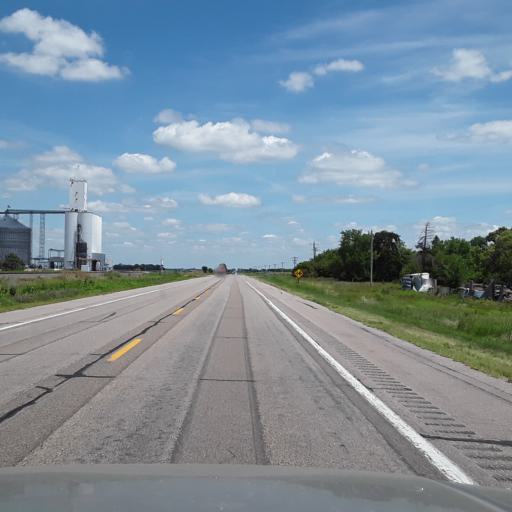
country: US
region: Nebraska
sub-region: Nance County
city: Genoa
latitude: 41.3258
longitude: -97.6400
